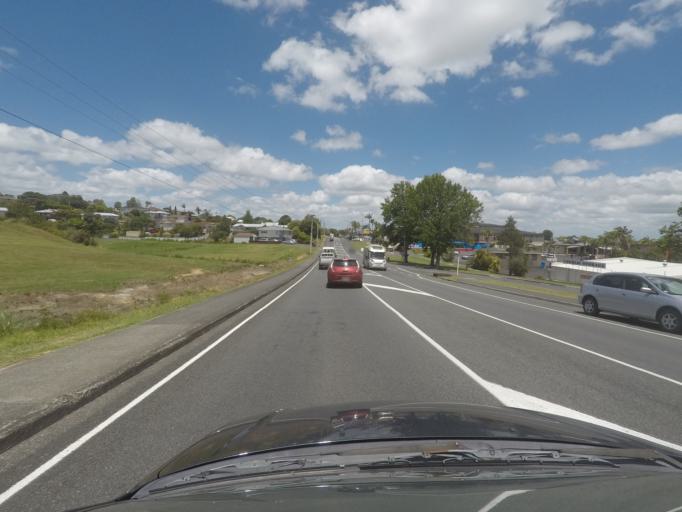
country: NZ
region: Northland
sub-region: Whangarei
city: Whangarei
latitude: -35.7528
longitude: 174.3682
